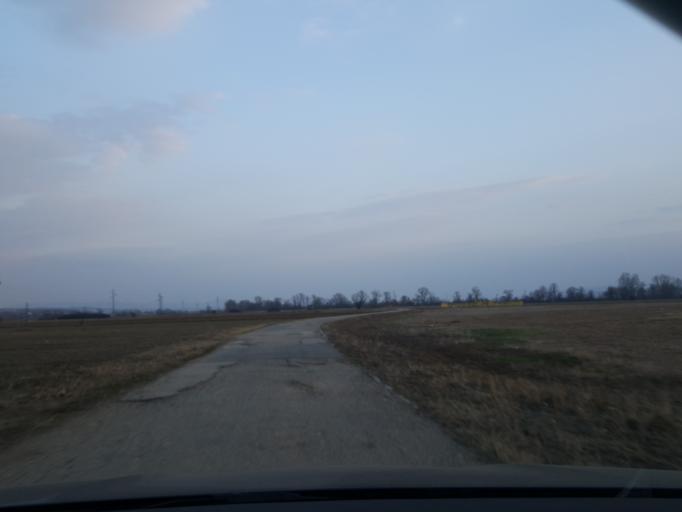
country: RS
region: Central Serbia
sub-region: Nisavski Okrug
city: Aleksinac
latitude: 43.5503
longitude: 21.6701
